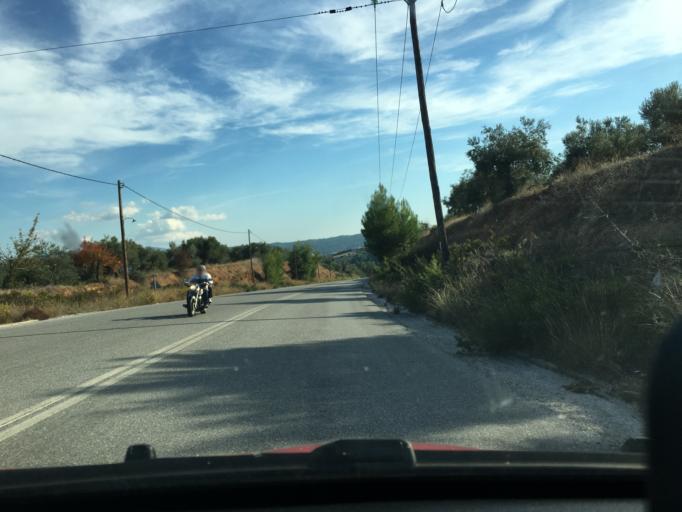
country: GR
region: Central Macedonia
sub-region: Nomos Chalkidikis
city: Agios Nikolaos
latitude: 40.2645
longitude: 23.6979
